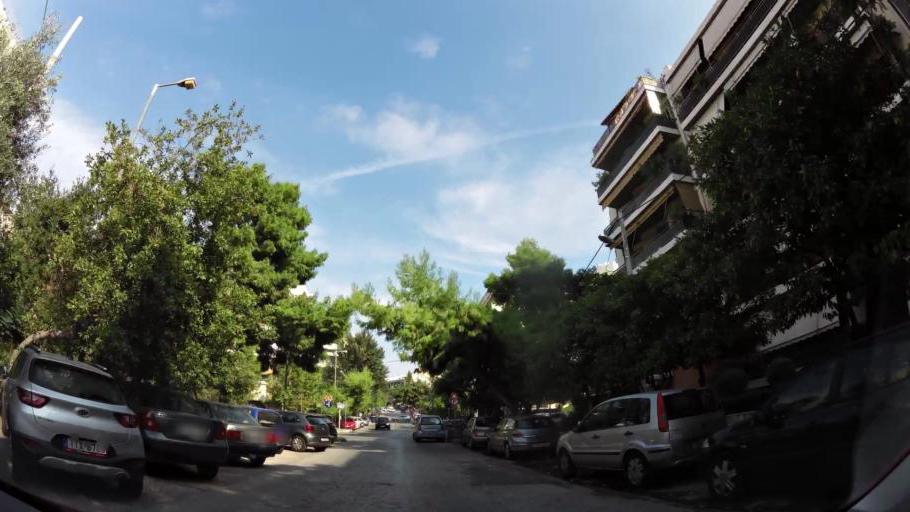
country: GR
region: Attica
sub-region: Nomarchia Athinas
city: Nea Smyrni
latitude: 37.9450
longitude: 23.7108
